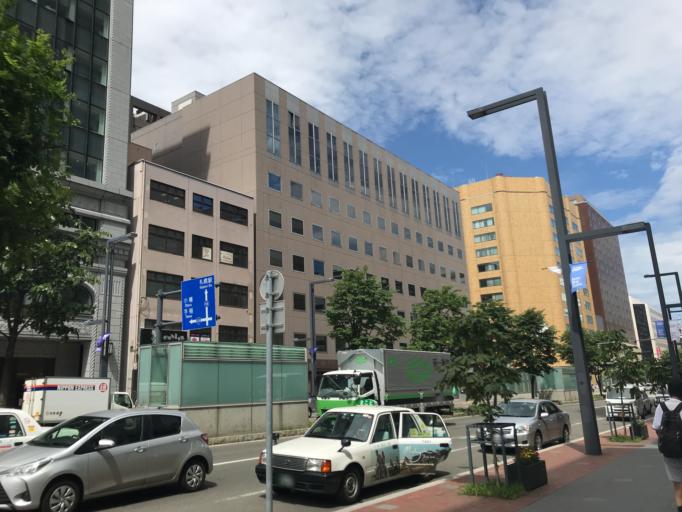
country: JP
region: Hokkaido
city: Sapporo
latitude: 43.0611
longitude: 141.3521
